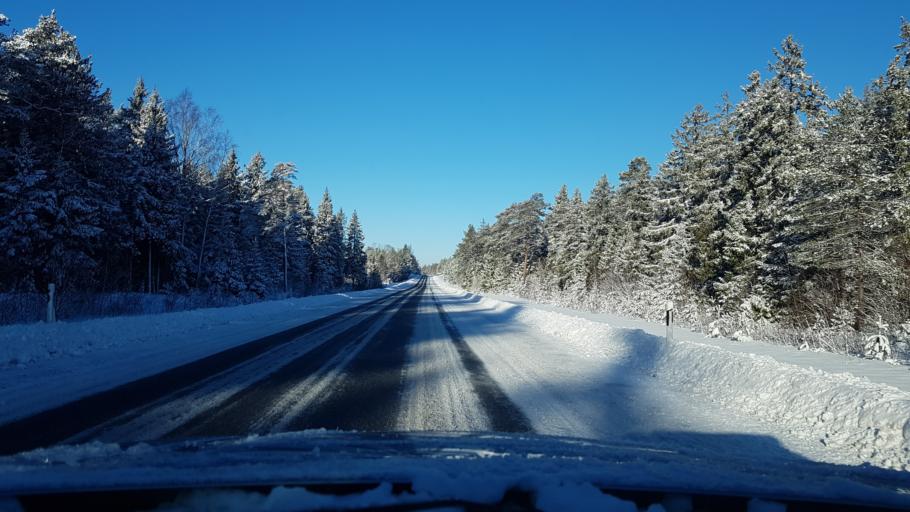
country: EE
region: Hiiumaa
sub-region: Kaerdla linn
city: Kardla
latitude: 58.9676
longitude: 22.8314
